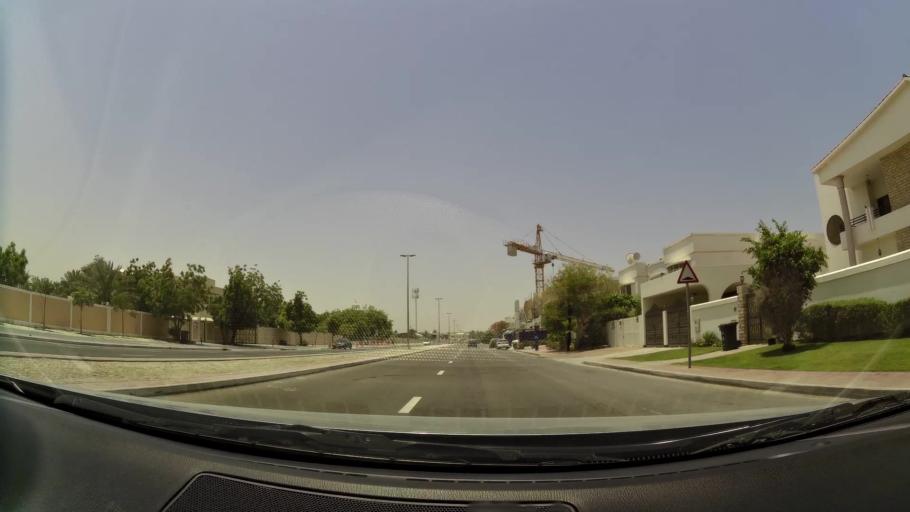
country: AE
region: Dubai
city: Dubai
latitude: 25.1875
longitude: 55.2337
